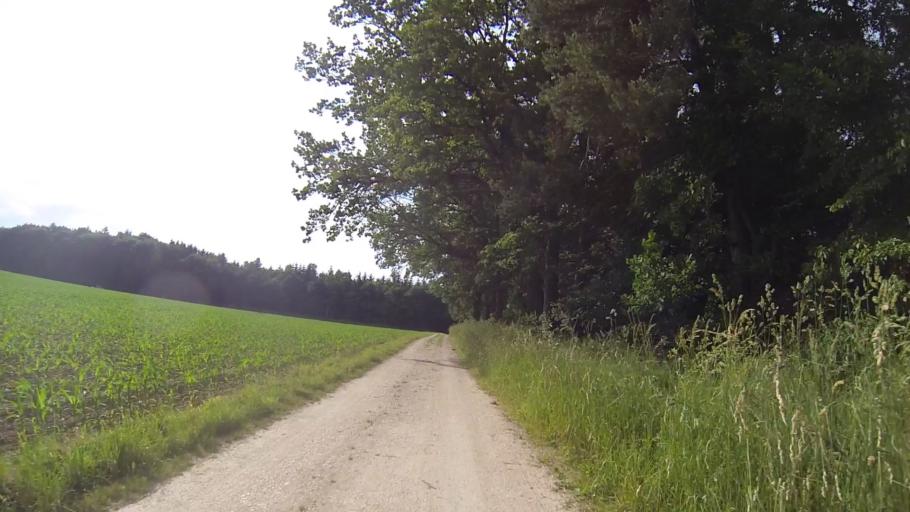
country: DE
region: Baden-Wuerttemberg
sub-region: Tuebingen Region
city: Staig
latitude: 48.3453
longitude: 9.9608
